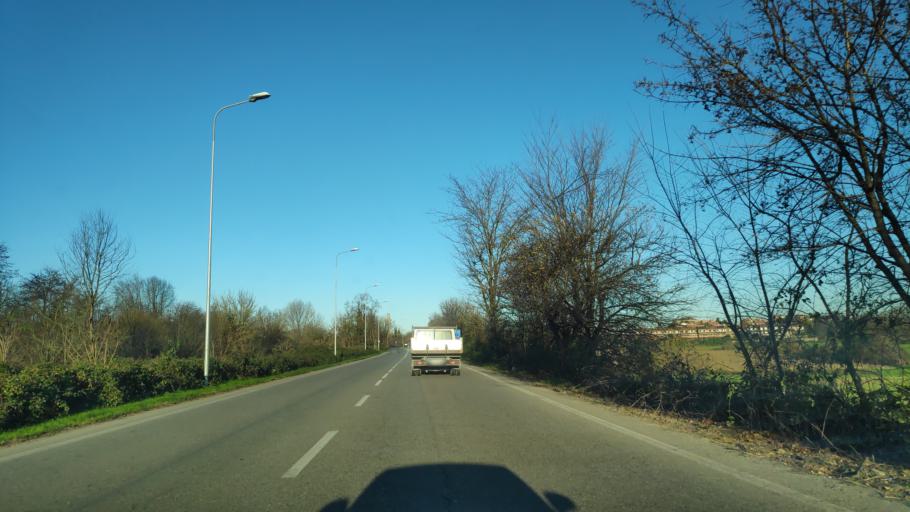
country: IT
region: Lombardy
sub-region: Citta metropolitana di Milano
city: Fizzonasco
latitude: 45.3625
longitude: 9.1925
